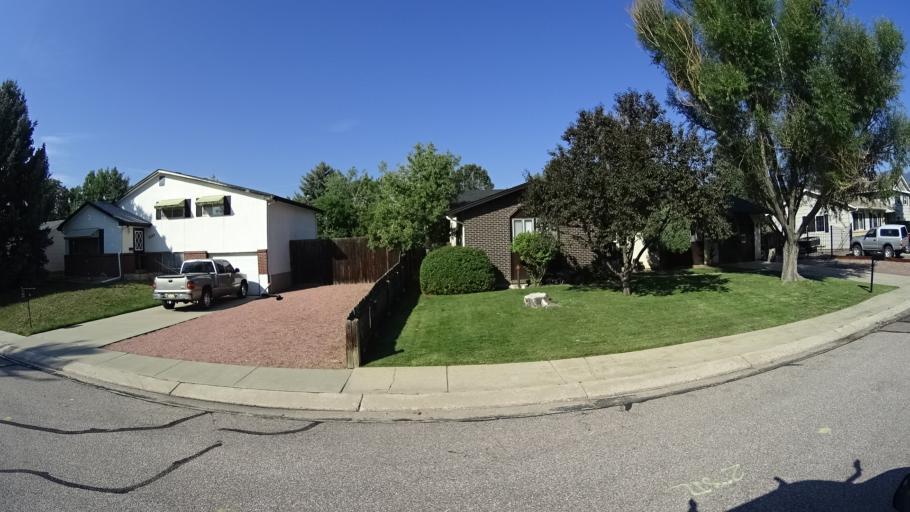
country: US
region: Colorado
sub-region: El Paso County
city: Colorado Springs
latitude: 38.8944
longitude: -104.8399
